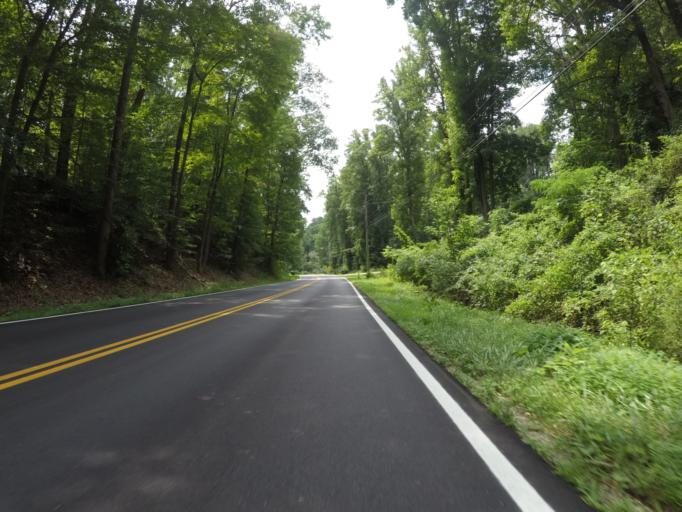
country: US
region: Kentucky
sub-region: Boyd County
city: Ashland
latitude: 38.4461
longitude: -82.6369
